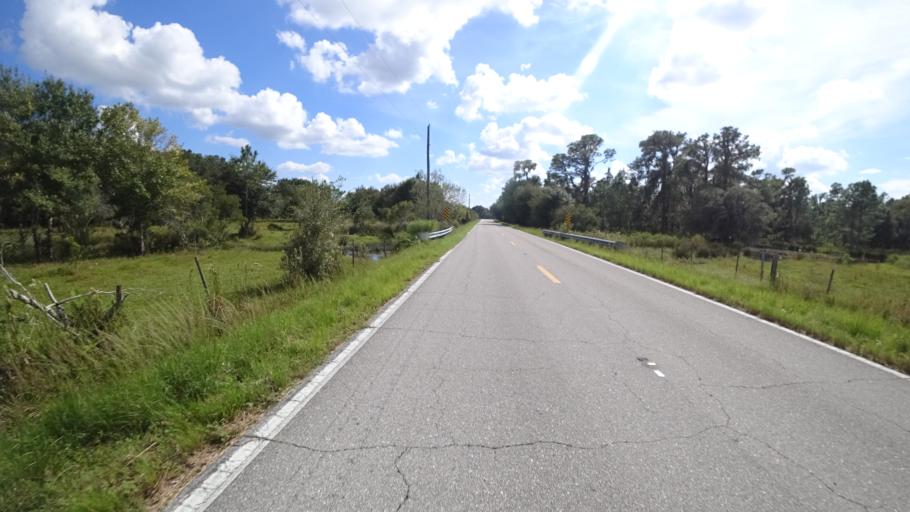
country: US
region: Florida
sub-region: Hardee County
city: Wauchula
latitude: 27.4973
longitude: -82.0708
